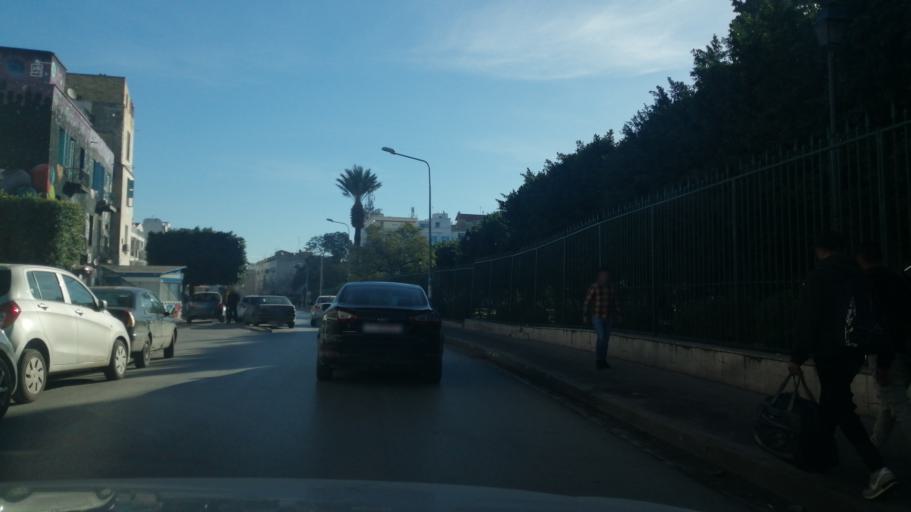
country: TN
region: Tunis
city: Tunis
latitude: 36.8055
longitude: 10.1783
